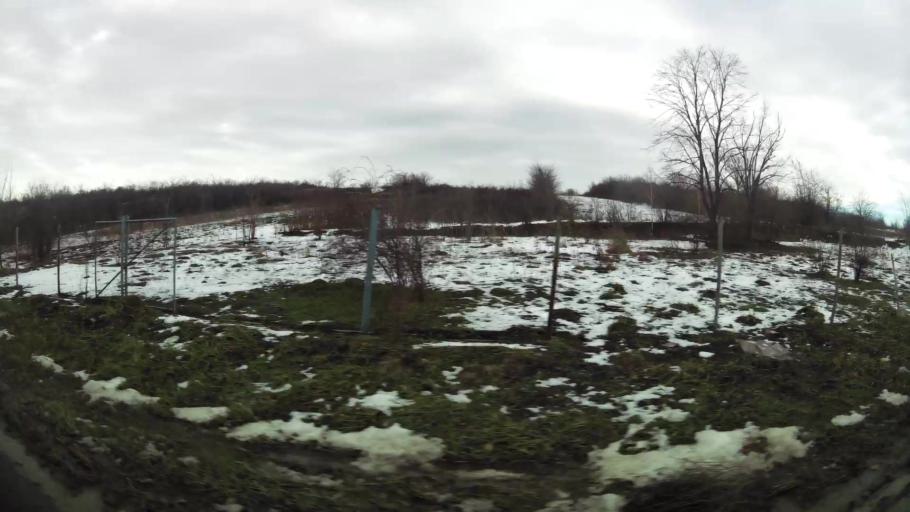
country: RS
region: Central Serbia
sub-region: Belgrade
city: Rakovica
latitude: 44.7226
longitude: 20.3996
